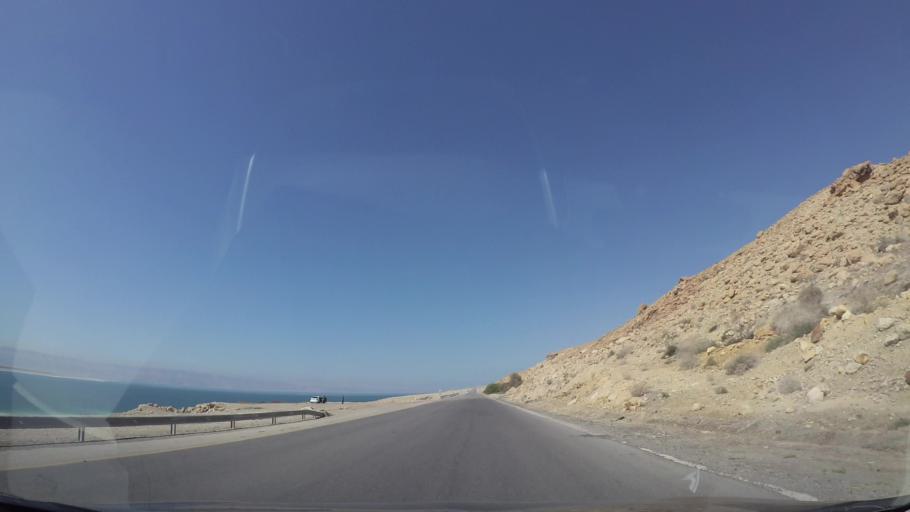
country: JO
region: Karak
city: Al Qasr
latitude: 31.3602
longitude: 35.5483
